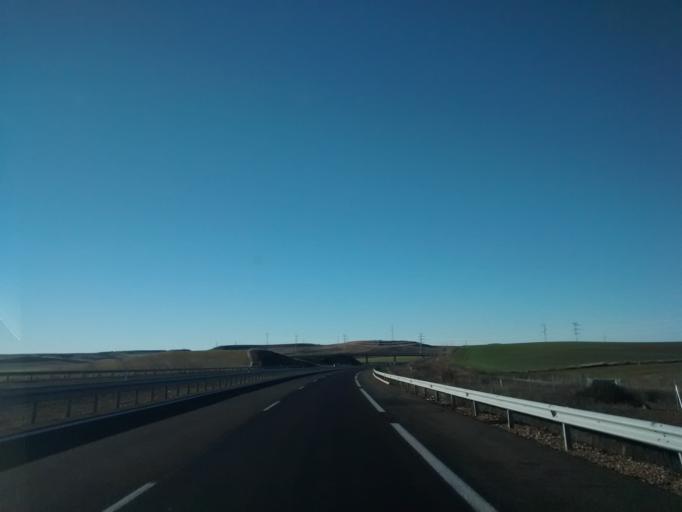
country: ES
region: Castille and Leon
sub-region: Provincia de Palencia
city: San Cristobal de Boedo
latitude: 42.5697
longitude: -4.3474
